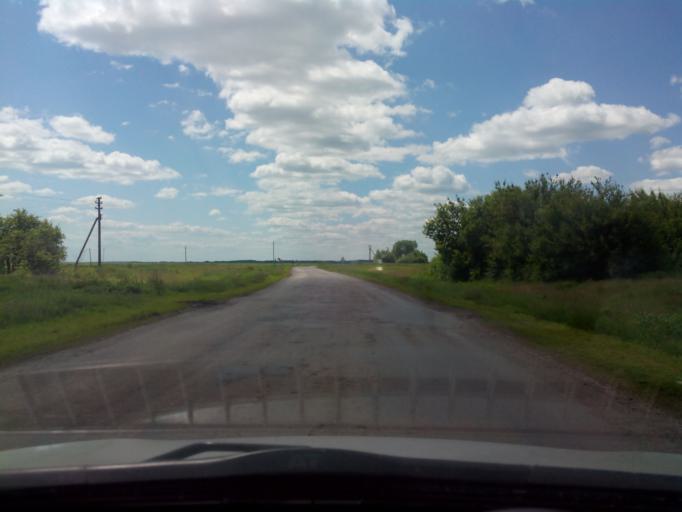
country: RU
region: Voronezj
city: Gribanovskiy
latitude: 51.6273
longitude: 41.8869
